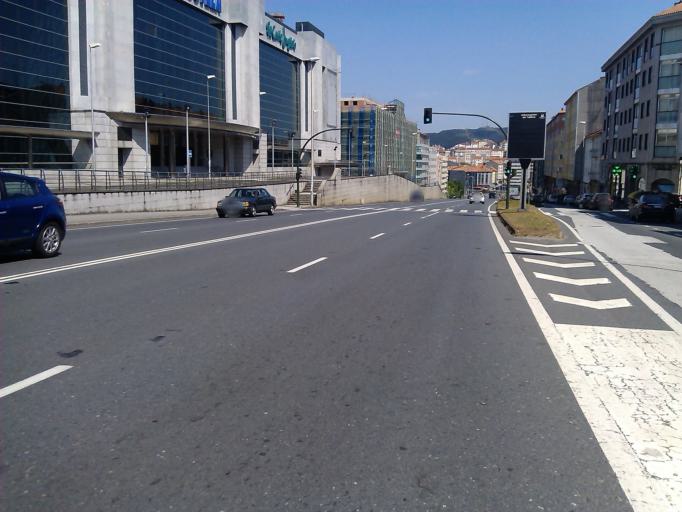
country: ES
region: Galicia
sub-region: Provincia da Coruna
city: Santiago de Compostela
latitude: 42.8623
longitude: -8.5416
